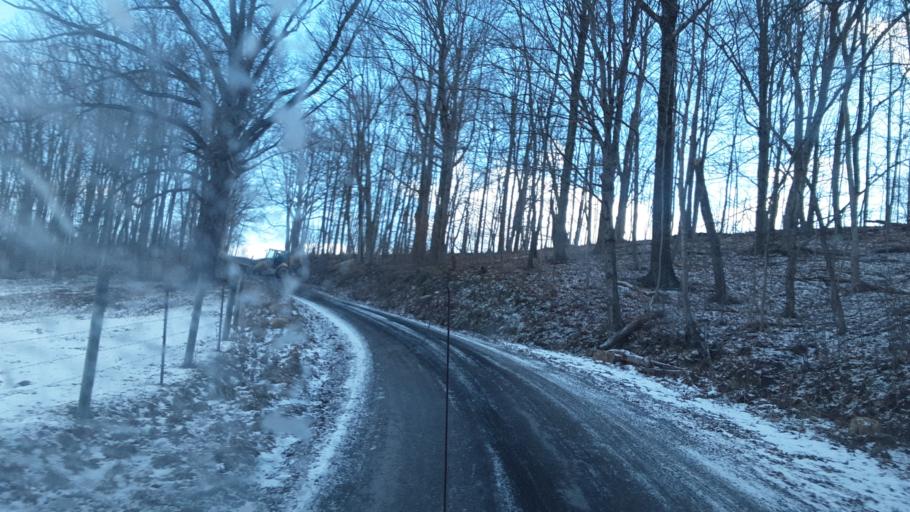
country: US
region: Ohio
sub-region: Carroll County
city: Carrollton
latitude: 40.5469
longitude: -81.0745
